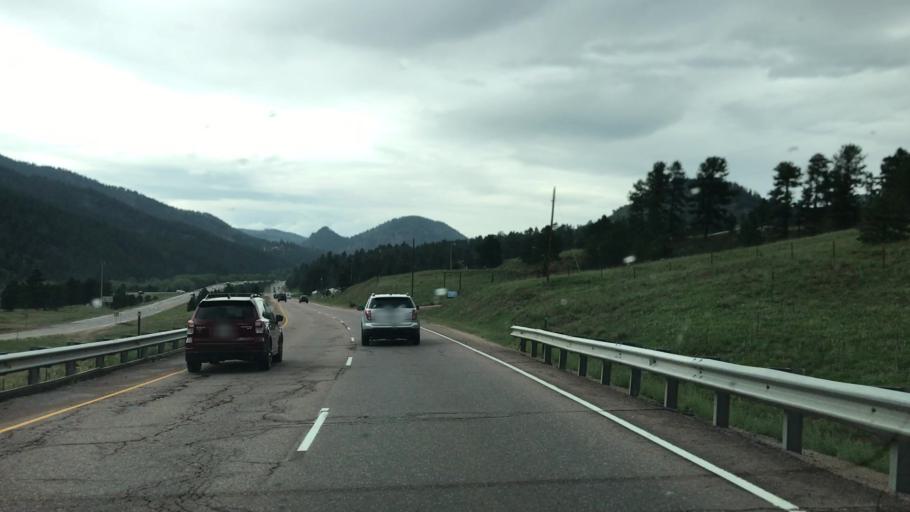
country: US
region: Colorado
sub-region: El Paso County
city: Cascade-Chipita Park
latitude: 38.9388
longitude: -105.0109
